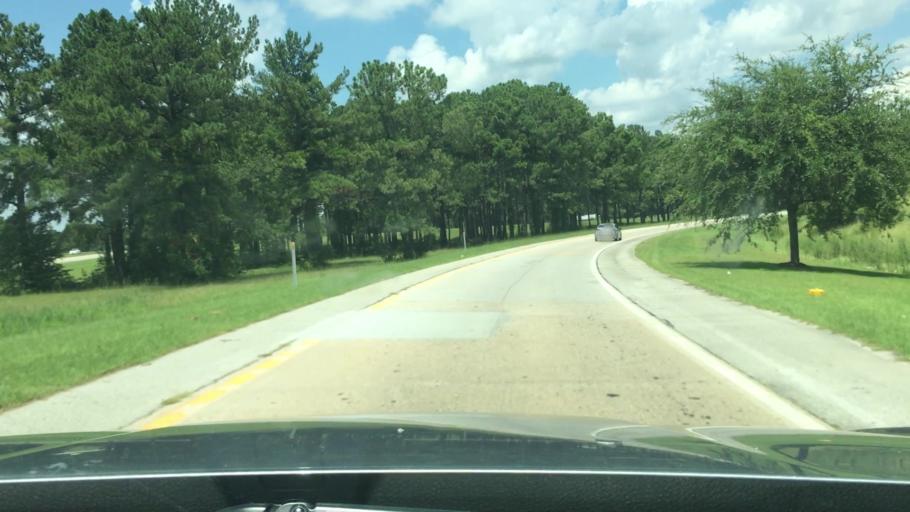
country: US
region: South Carolina
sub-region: Florence County
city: Florence
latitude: 34.1914
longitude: -79.8405
